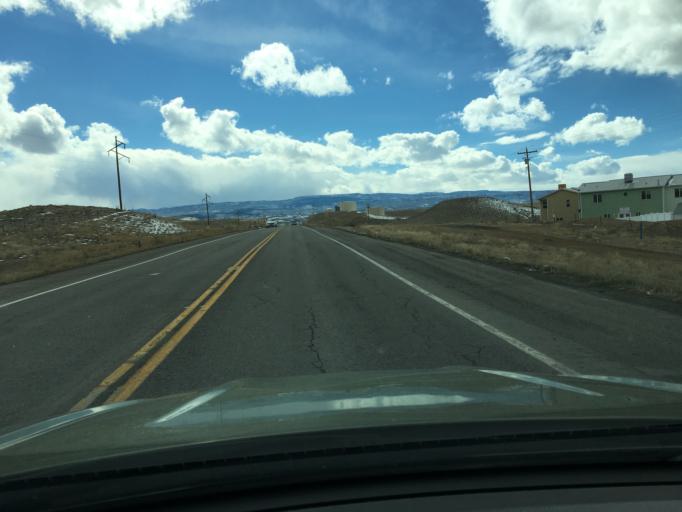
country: US
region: Colorado
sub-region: Mesa County
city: Fruitvale
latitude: 39.0213
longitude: -108.4669
